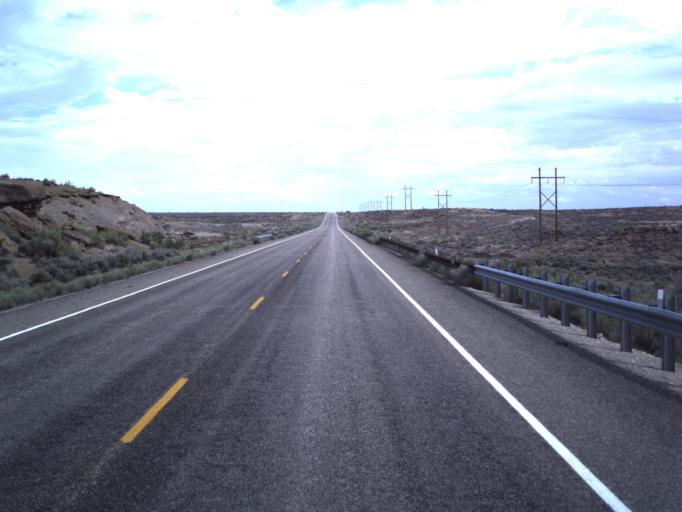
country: US
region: Colorado
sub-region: Rio Blanco County
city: Rangely
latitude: 40.0889
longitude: -109.2210
